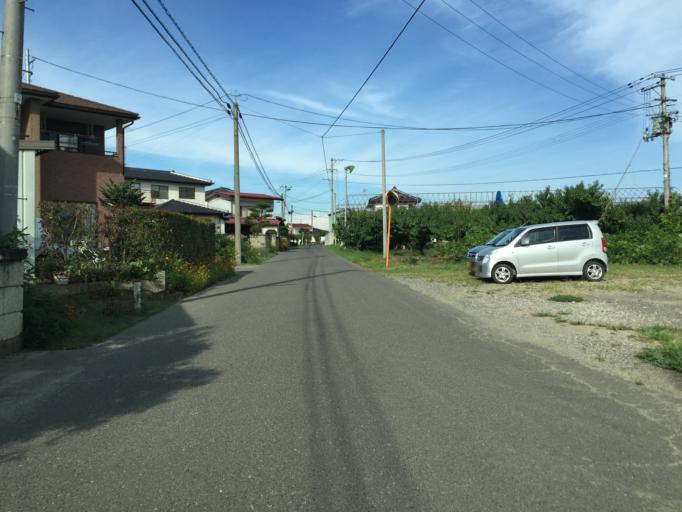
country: JP
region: Fukushima
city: Hobaramachi
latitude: 37.8225
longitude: 140.5199
